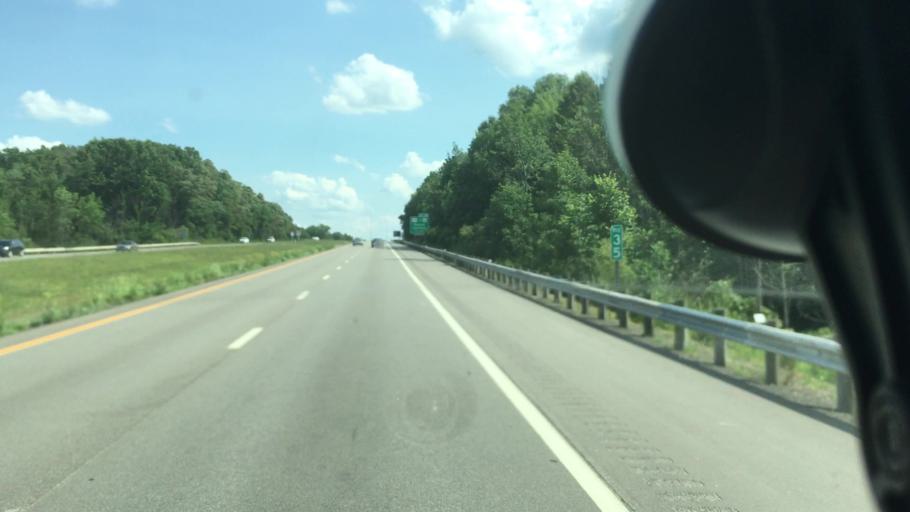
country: US
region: Ohio
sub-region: Mahoning County
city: Canfield
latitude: 41.0381
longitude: -80.7425
